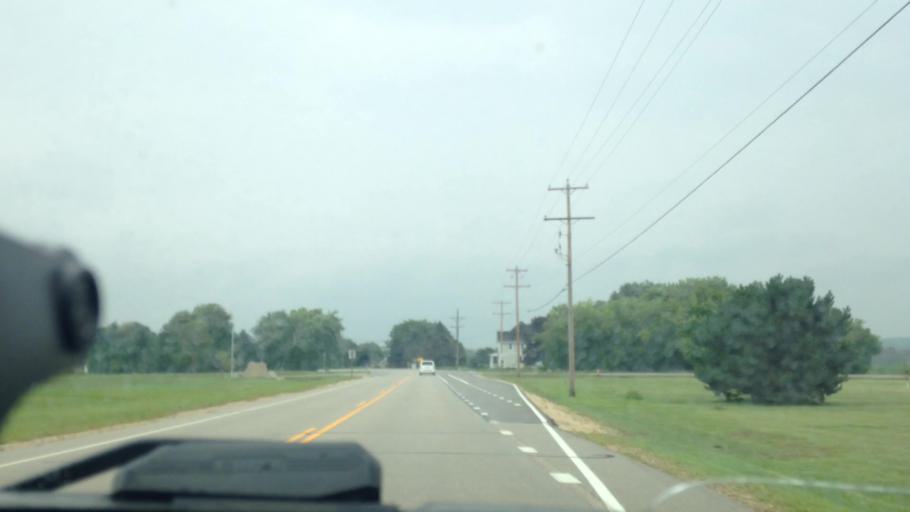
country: US
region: Wisconsin
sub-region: Washington County
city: Slinger
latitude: 43.3478
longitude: -88.3115
